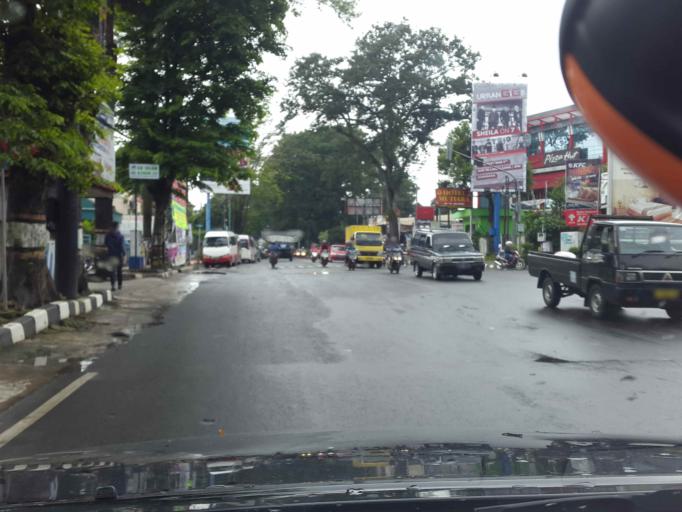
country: ID
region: Central Java
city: Salatiga
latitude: -7.3190
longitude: 110.4972
